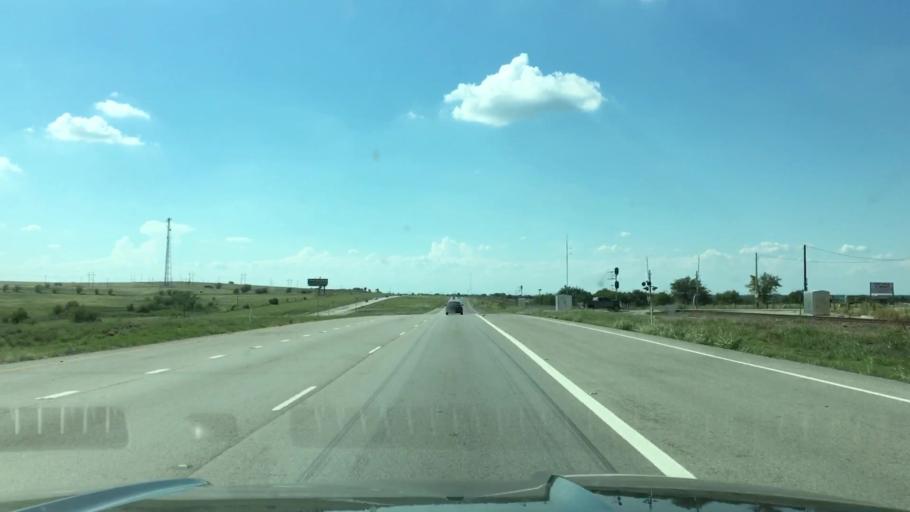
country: US
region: Texas
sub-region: Wise County
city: New Fairview
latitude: 33.1508
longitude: -97.5078
